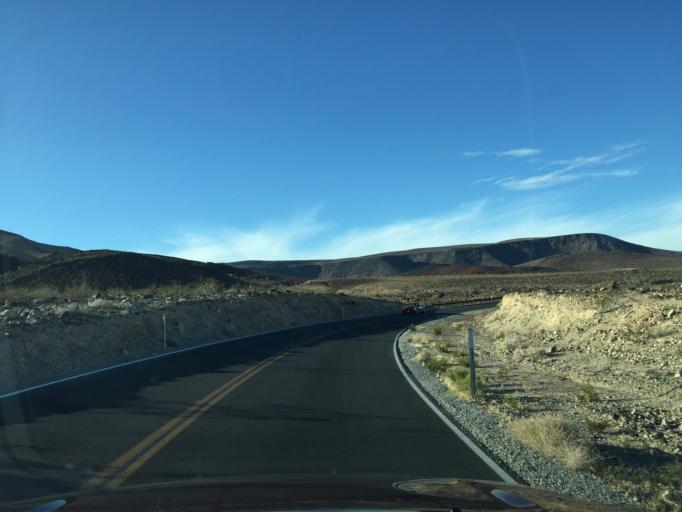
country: US
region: California
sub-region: San Bernardino County
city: Searles Valley
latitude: 36.3484
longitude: -117.5277
